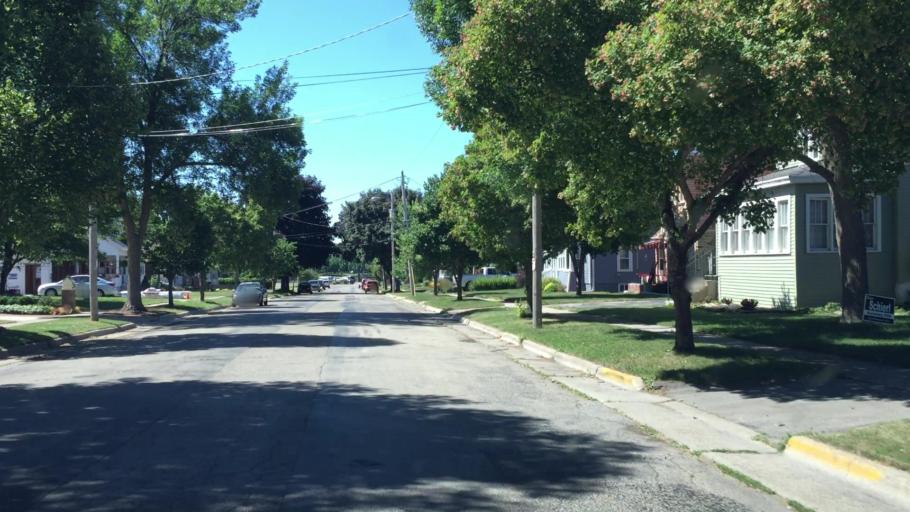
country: US
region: Wisconsin
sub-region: Winnebago County
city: Neenah
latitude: 44.1876
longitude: -88.4497
